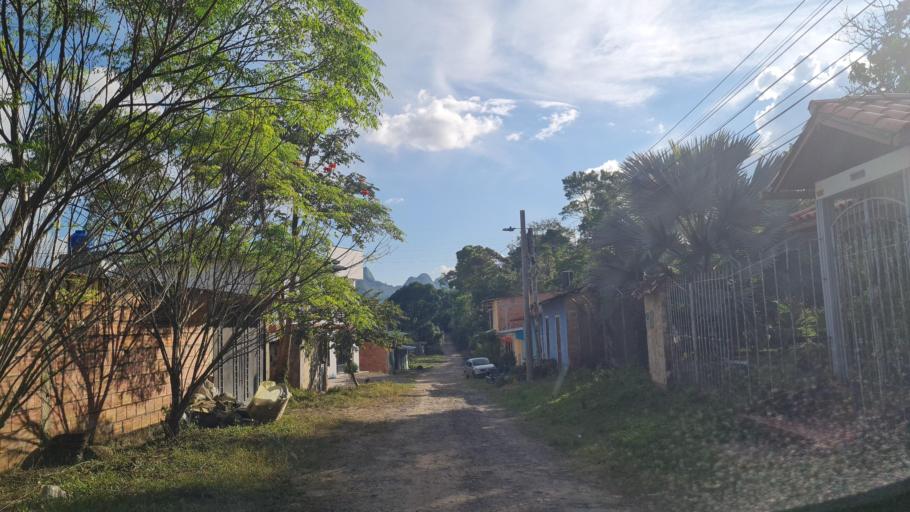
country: CO
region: Boyaca
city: San Luis de Gaceno
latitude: 4.8266
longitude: -73.1647
